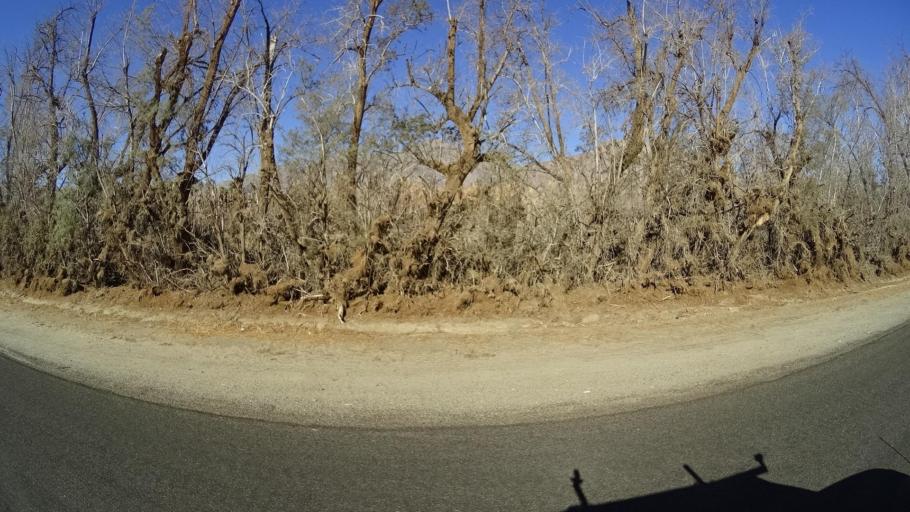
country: US
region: California
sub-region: San Diego County
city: Borrego Springs
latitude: 33.2731
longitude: -116.3750
